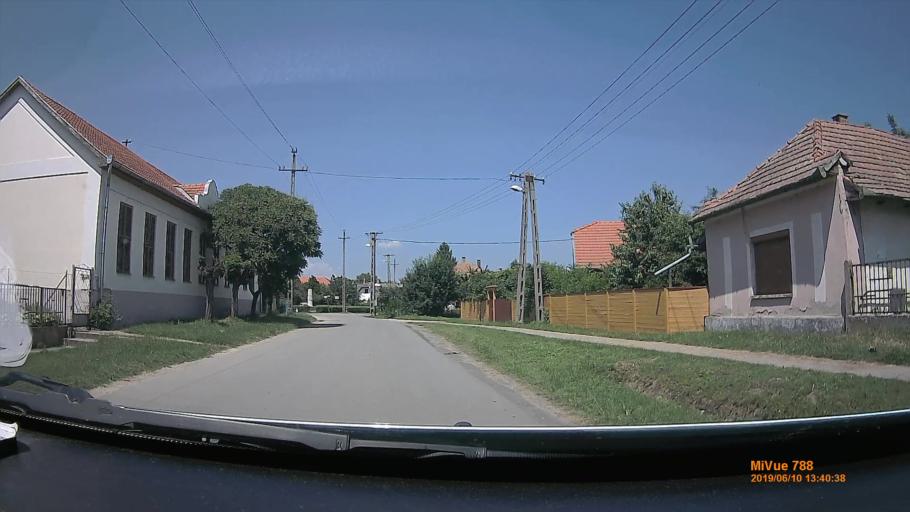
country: HU
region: Szabolcs-Szatmar-Bereg
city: Tiszadob
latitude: 48.0114
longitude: 21.1674
